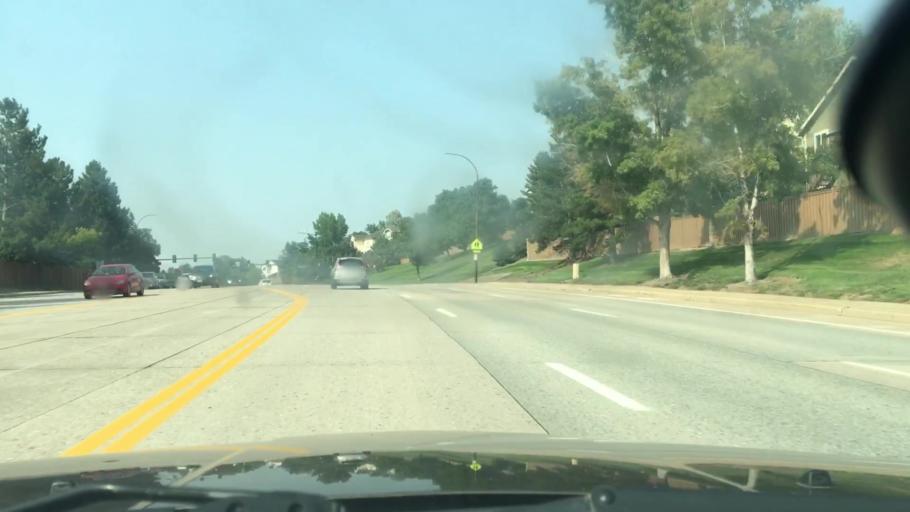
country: US
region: Colorado
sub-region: Douglas County
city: Carriage Club
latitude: 39.5452
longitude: -104.9103
